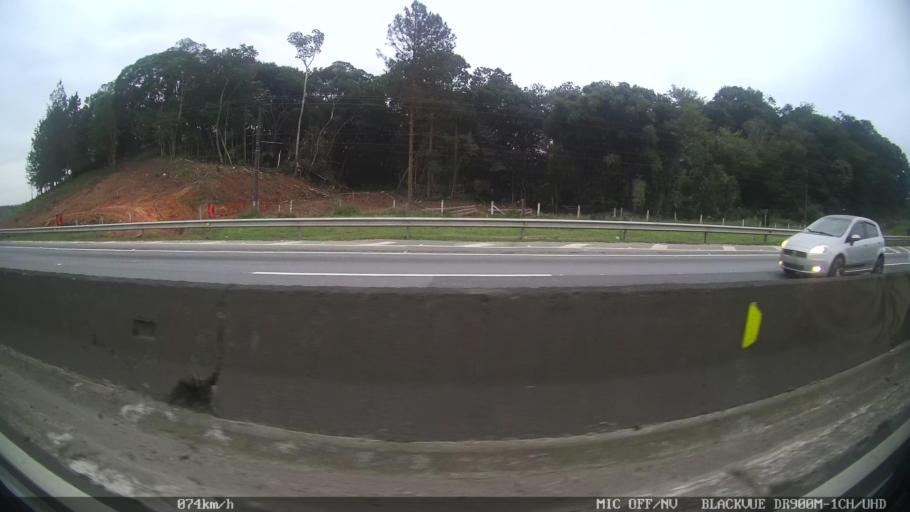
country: BR
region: Santa Catarina
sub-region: Joinville
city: Joinville
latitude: -26.4618
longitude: -48.7537
